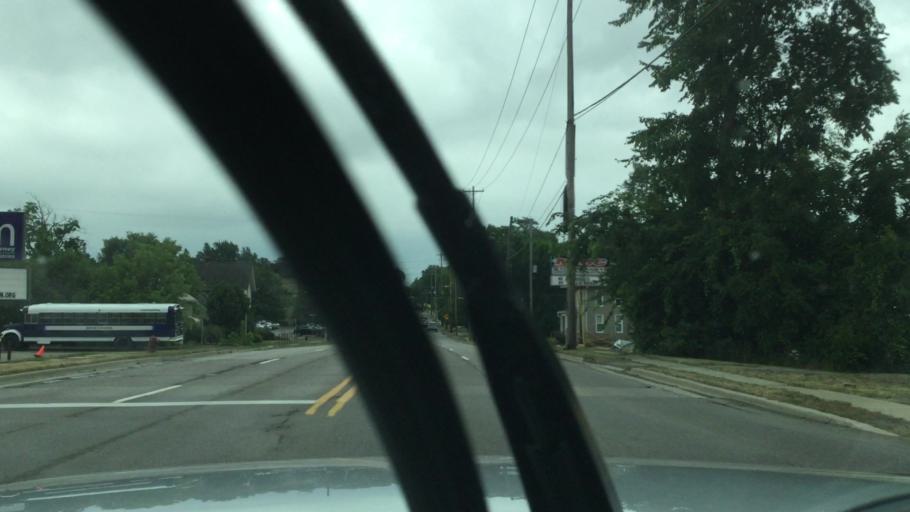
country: US
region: Michigan
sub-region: Genesee County
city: Davison
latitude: 43.0303
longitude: -83.5180
